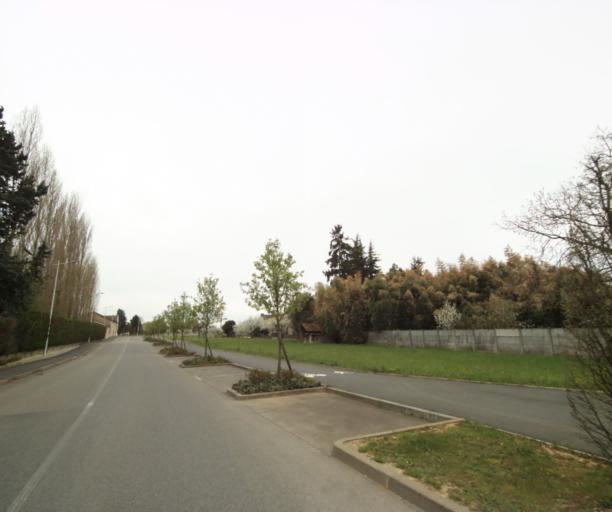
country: FR
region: Bourgogne
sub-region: Departement de Saone-et-Loire
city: Charnay-les-Macon
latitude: 46.3112
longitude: 4.8018
